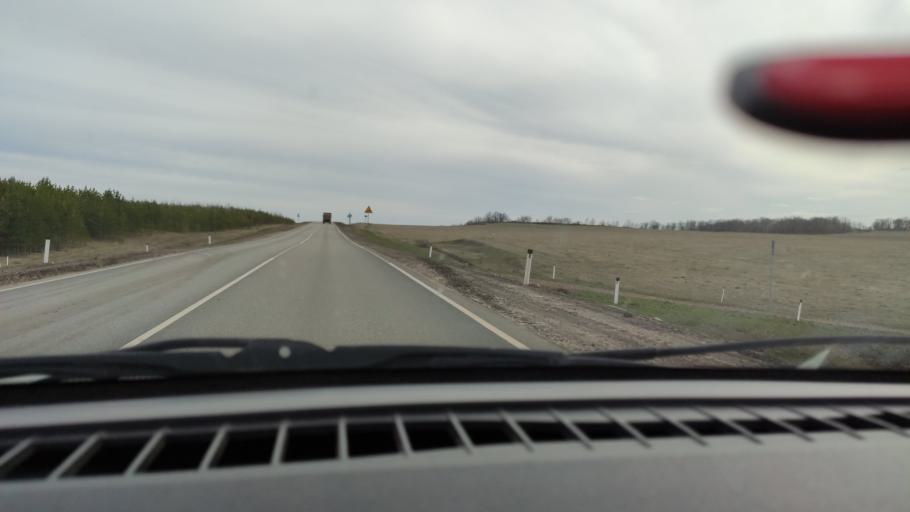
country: RU
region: Bashkortostan
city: Yermolayevo
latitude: 52.7248
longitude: 55.8569
